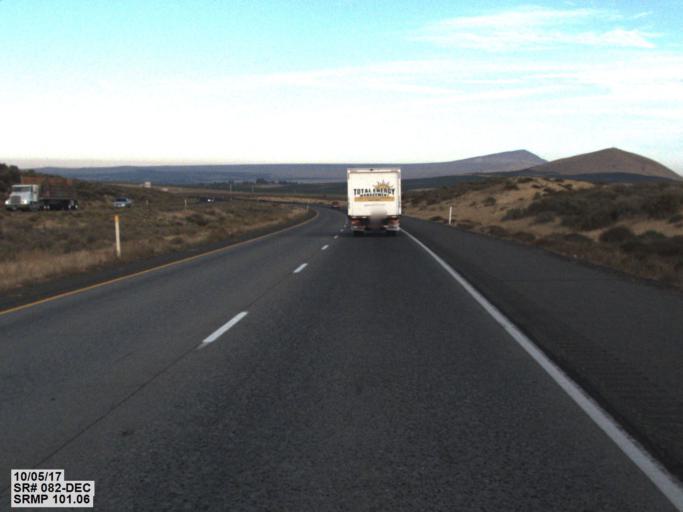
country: US
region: Washington
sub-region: Benton County
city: West Richland
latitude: 46.2583
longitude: -119.3853
